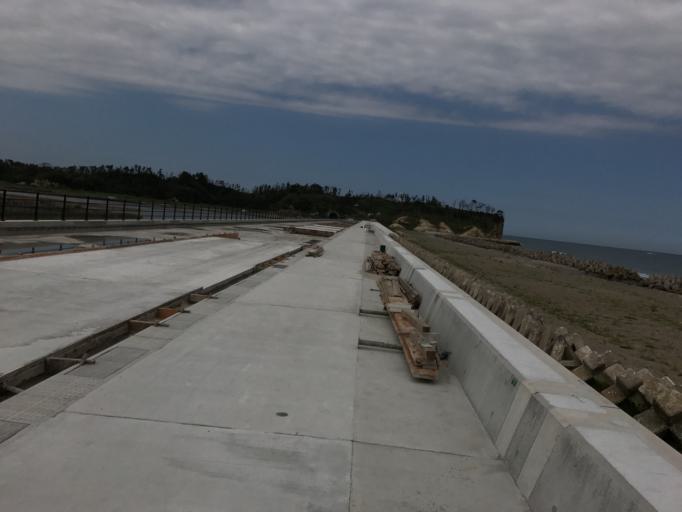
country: JP
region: Miyagi
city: Marumori
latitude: 37.8179
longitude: 140.9856
